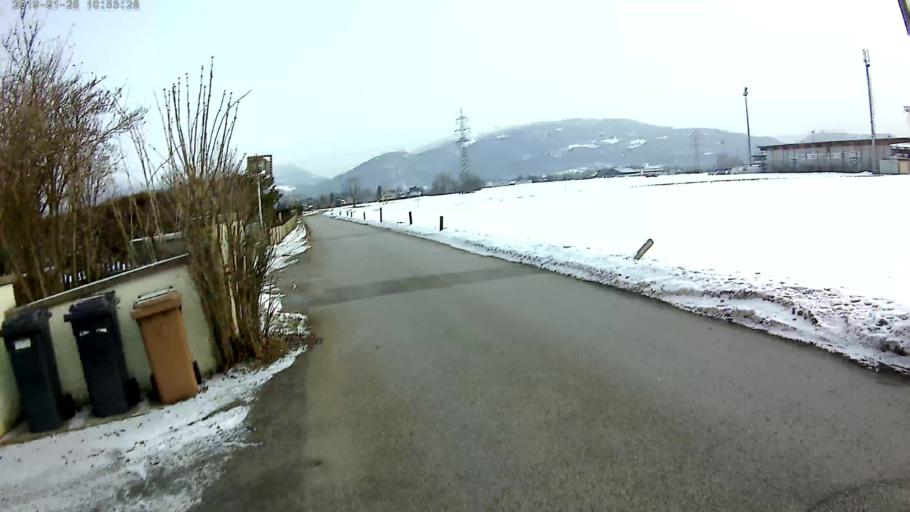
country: AT
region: Salzburg
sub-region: Politischer Bezirk Salzburg-Umgebung
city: Grodig
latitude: 47.7442
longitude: 13.0451
